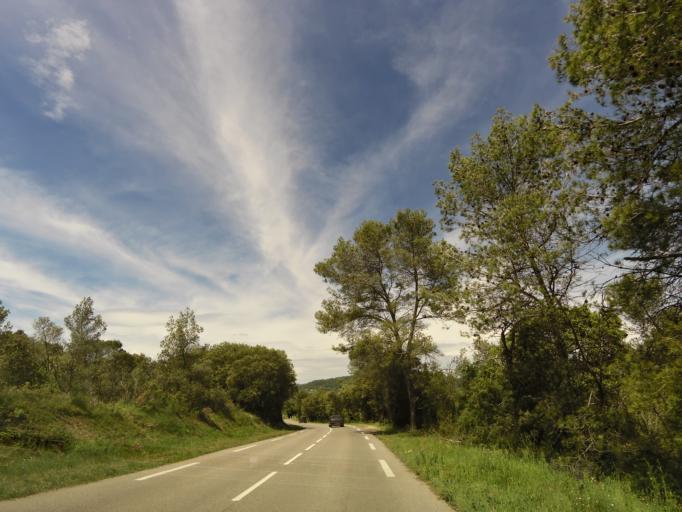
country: FR
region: Languedoc-Roussillon
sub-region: Departement du Gard
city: Sommieres
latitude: 43.8248
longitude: 4.0513
